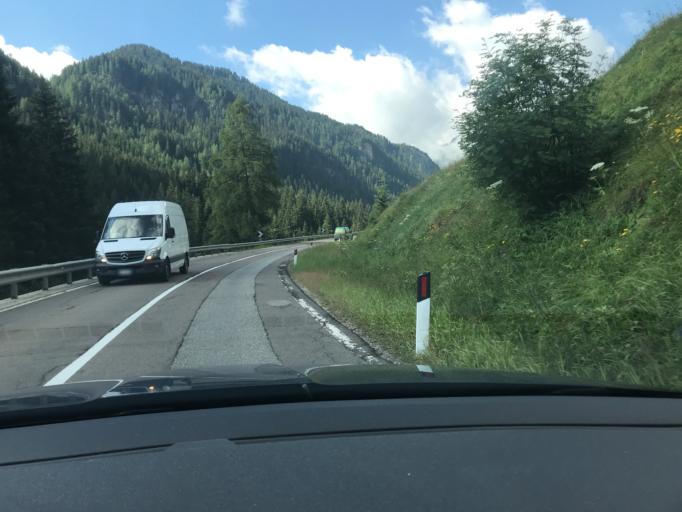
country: IT
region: Trentino-Alto Adige
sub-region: Bolzano
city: Corvara in Badia
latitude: 46.5698
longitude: 11.8907
